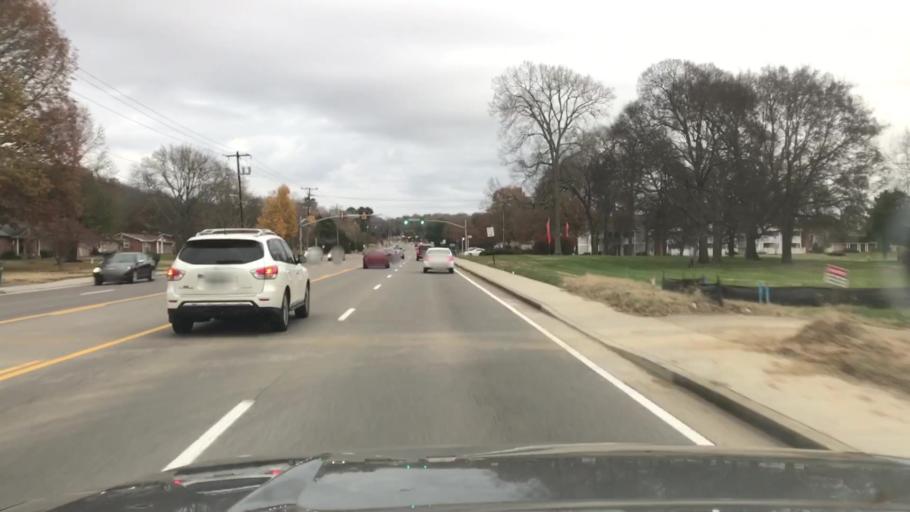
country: US
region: Tennessee
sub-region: Davidson County
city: Belle Meade
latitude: 36.0758
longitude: -86.9419
